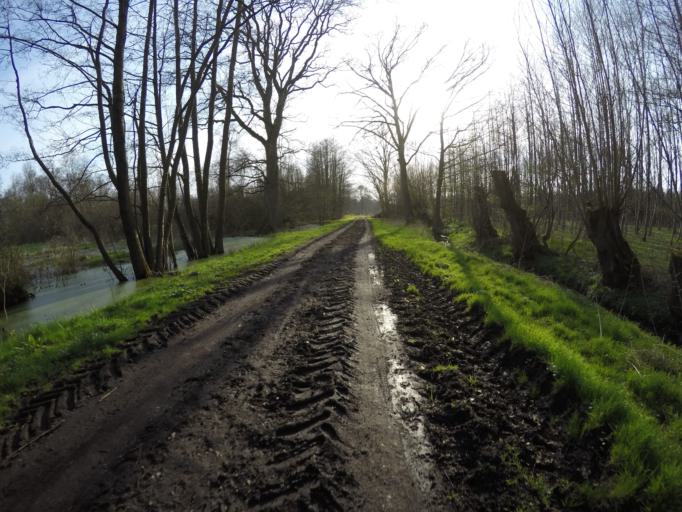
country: DE
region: Schleswig-Holstein
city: Hemdingen
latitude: 53.7490
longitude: 9.8503
